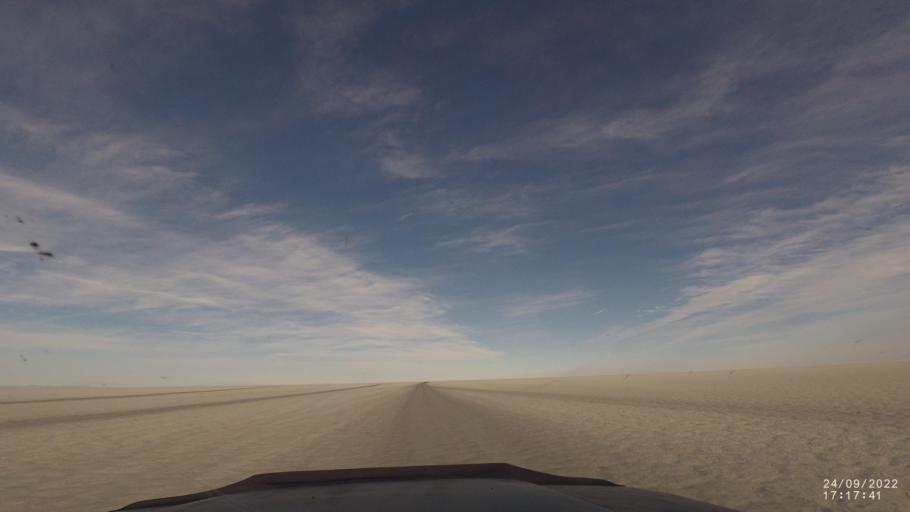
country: BO
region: Potosi
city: Colchani
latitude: -20.2392
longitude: -67.6205
